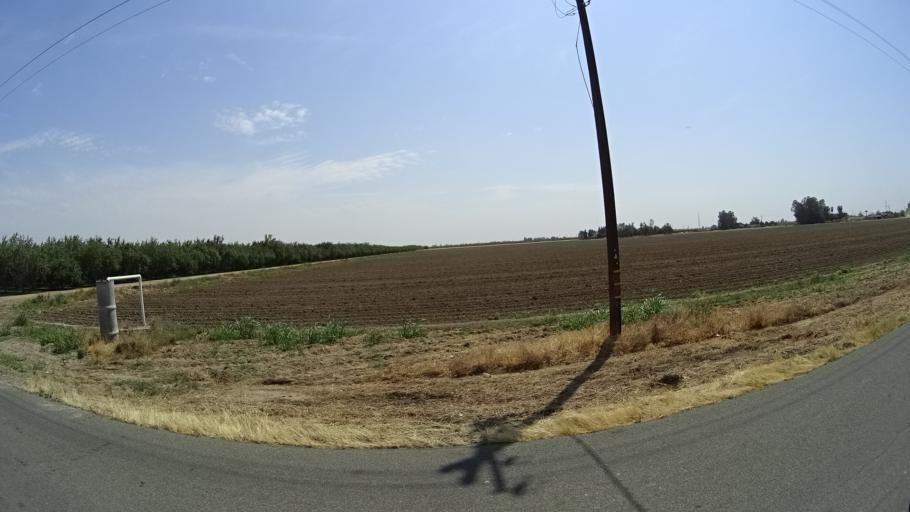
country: US
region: California
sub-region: Kings County
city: Armona
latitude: 36.3168
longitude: -119.7448
